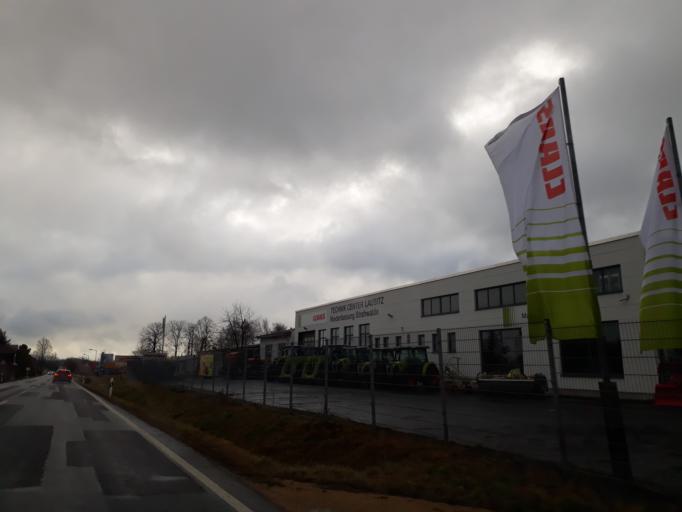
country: DE
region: Saxony
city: Herrnhut
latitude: 51.0318
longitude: 14.7182
